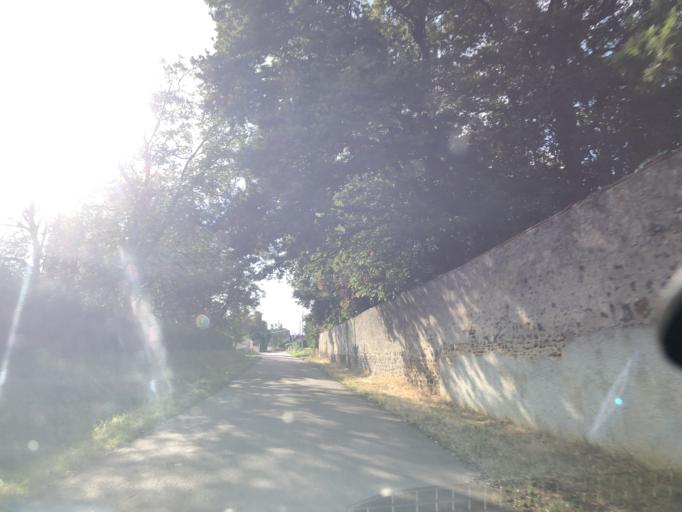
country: FR
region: Bourgogne
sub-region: Departement de l'Yonne
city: Charbuy
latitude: 47.8229
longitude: 3.4639
